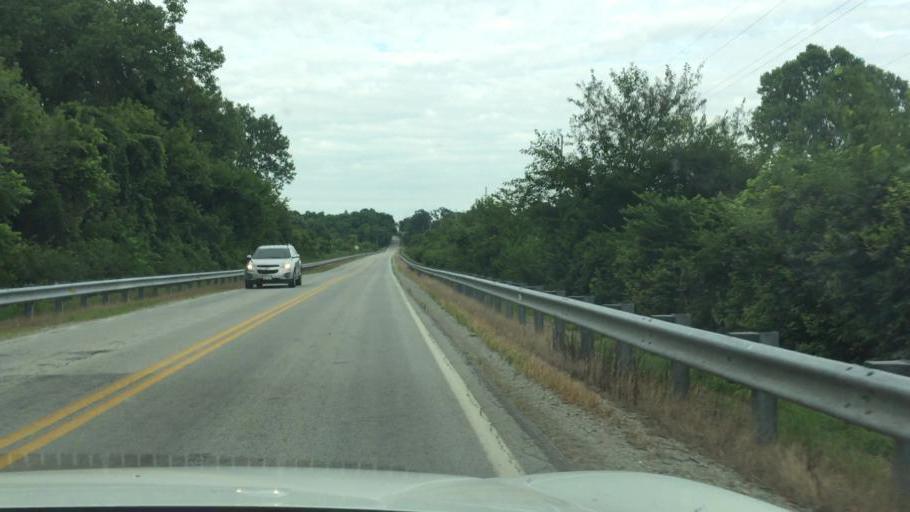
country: US
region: Ohio
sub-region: Clark County
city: Northridge
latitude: 39.9918
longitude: -83.7118
